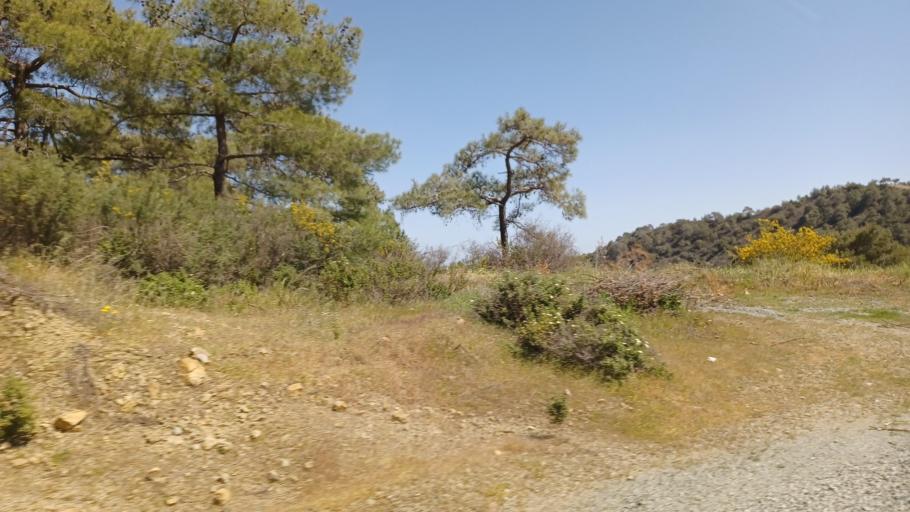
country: CY
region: Limassol
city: Parekklisha
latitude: 34.7995
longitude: 33.1365
